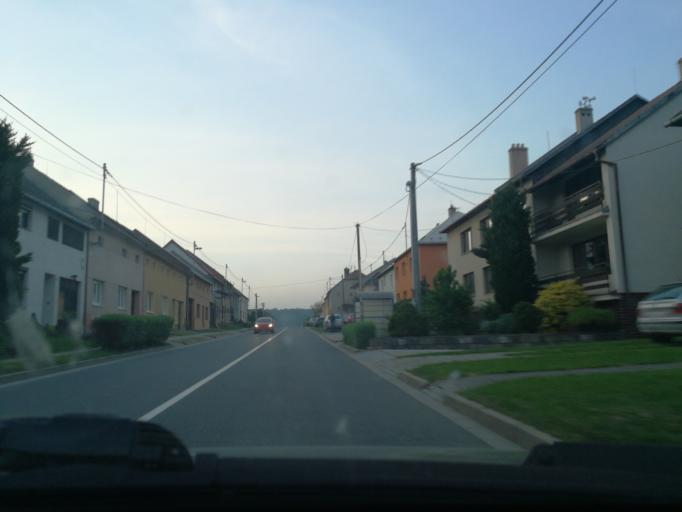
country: CZ
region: Zlin
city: Tlumacov
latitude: 49.2725
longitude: 17.5498
